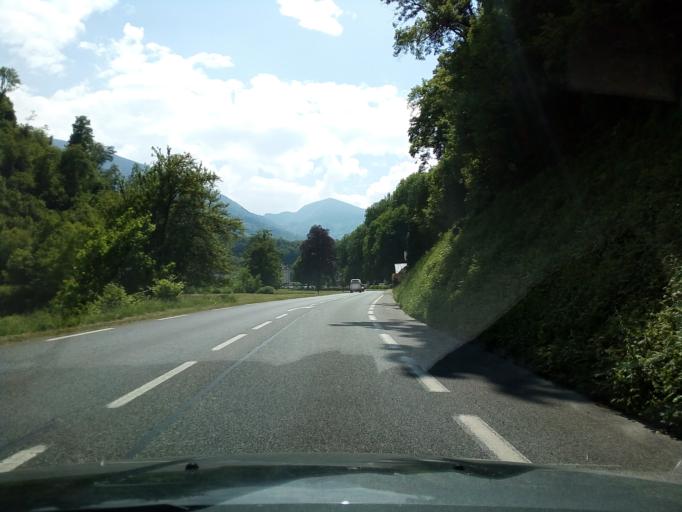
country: FR
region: Rhone-Alpes
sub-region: Departement de l'Isere
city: Vaulnaveys-le-Haut
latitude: 45.1468
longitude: 5.8286
